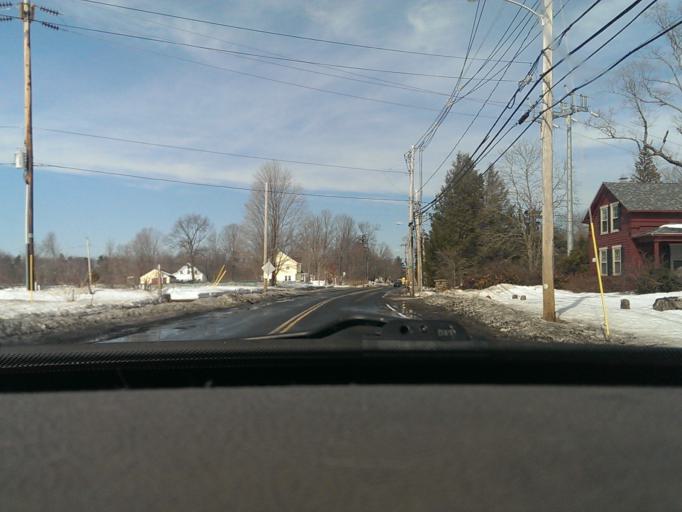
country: US
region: Massachusetts
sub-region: Hampden County
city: Wilbraham
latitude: 42.1102
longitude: -72.4357
